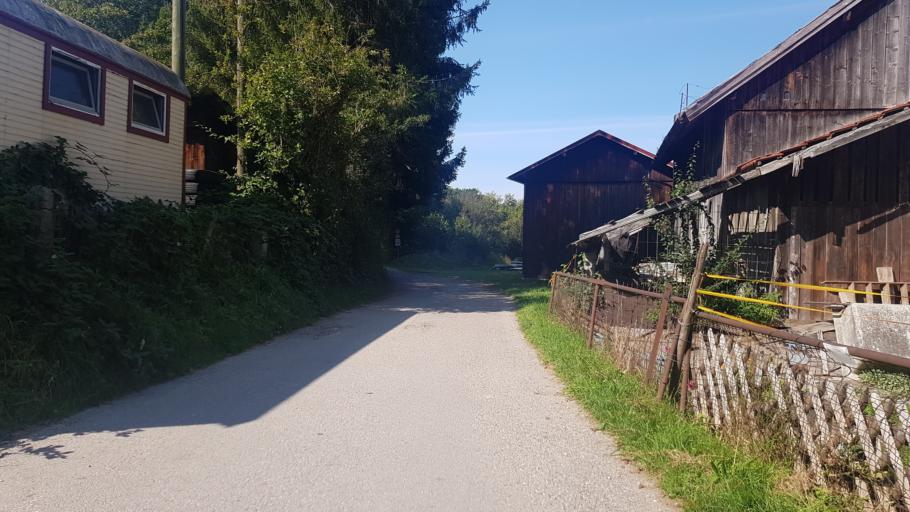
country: DE
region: Bavaria
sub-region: Upper Bavaria
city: Herrsching am Ammersee
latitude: 48.0131
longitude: 11.1577
